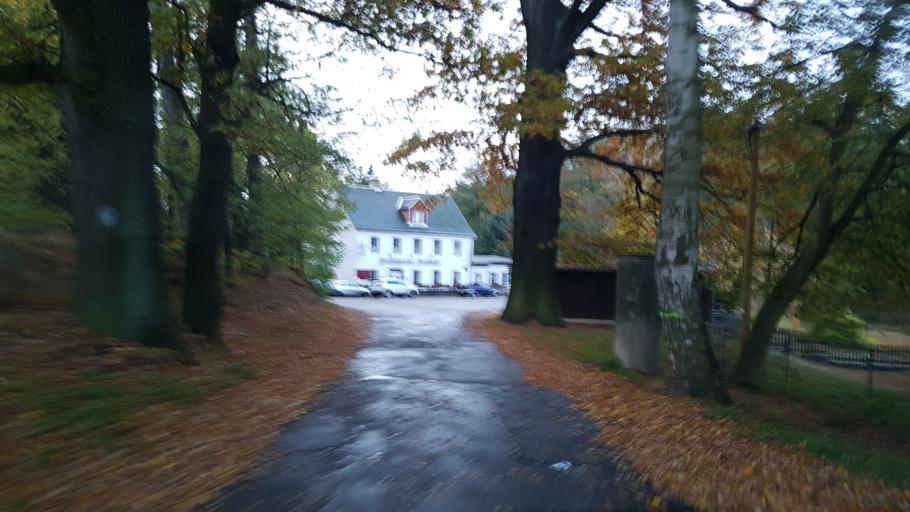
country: DE
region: Saxony
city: Cavertitz
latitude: 51.4137
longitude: 13.0689
